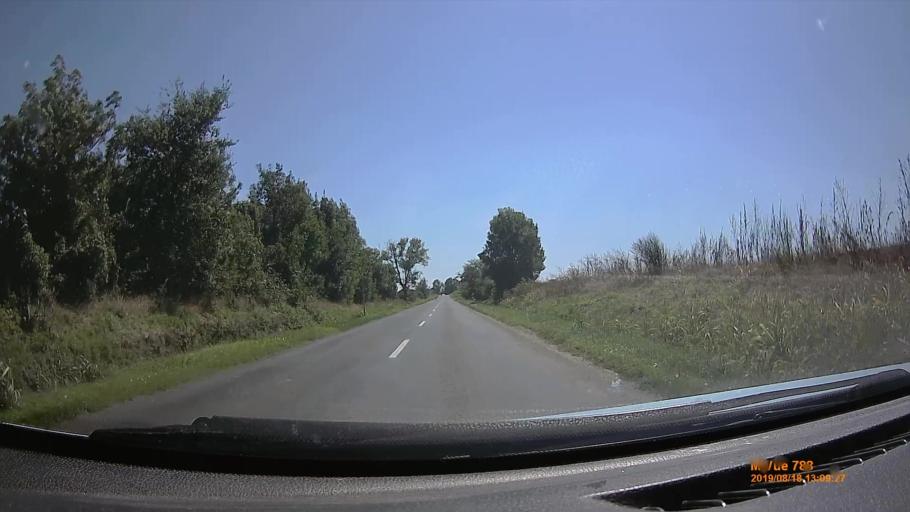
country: HU
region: Fejer
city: Kaloz
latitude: 46.9266
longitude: 18.5105
